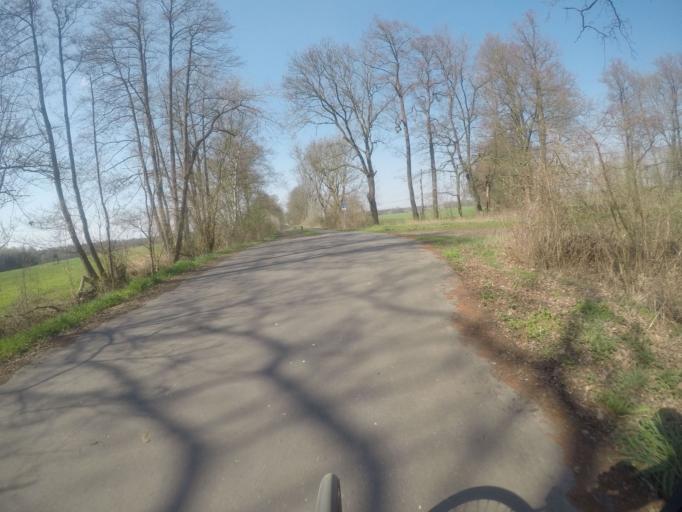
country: DE
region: Brandenburg
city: Falkensee
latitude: 52.6295
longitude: 13.0971
